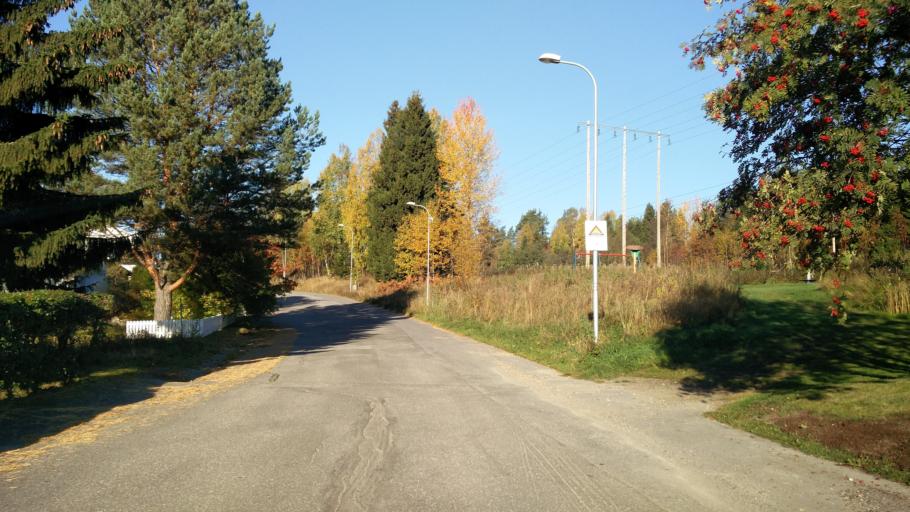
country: SE
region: Vaesternorrland
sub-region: Sundsvalls Kommun
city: Sundsvall
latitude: 62.4073
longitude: 17.2618
